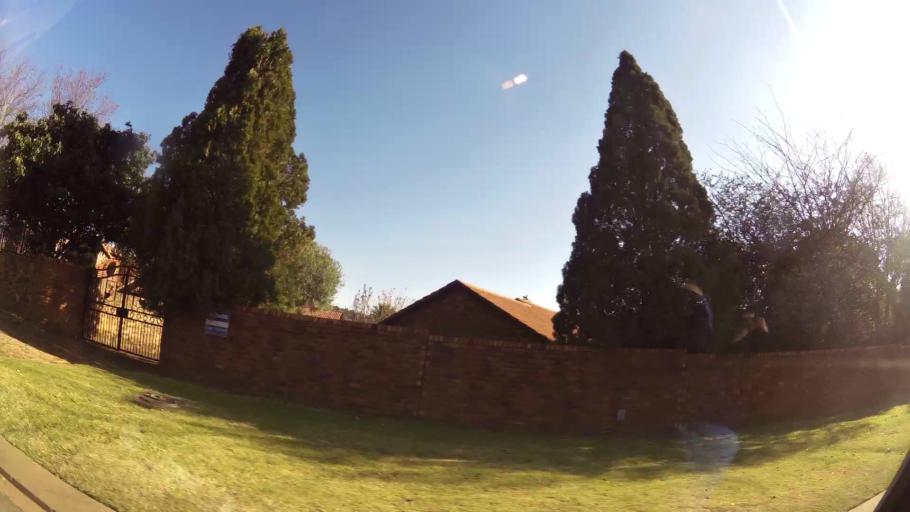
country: ZA
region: Gauteng
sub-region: City of Johannesburg Metropolitan Municipality
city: Johannesburg
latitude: -26.2833
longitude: 28.0671
